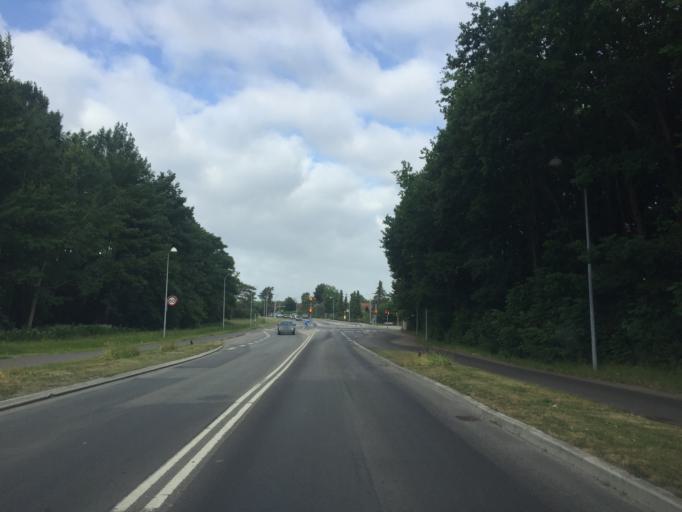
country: DK
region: Capital Region
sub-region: Rodovre Kommune
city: Rodovre
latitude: 55.6578
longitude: 12.4477
